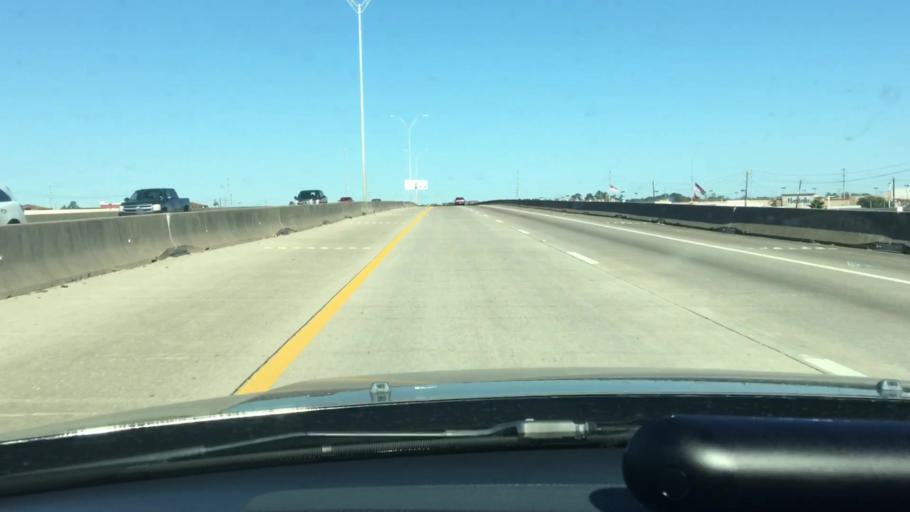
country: US
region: Texas
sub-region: Harris County
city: Cloverleaf
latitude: 29.8072
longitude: -95.1633
